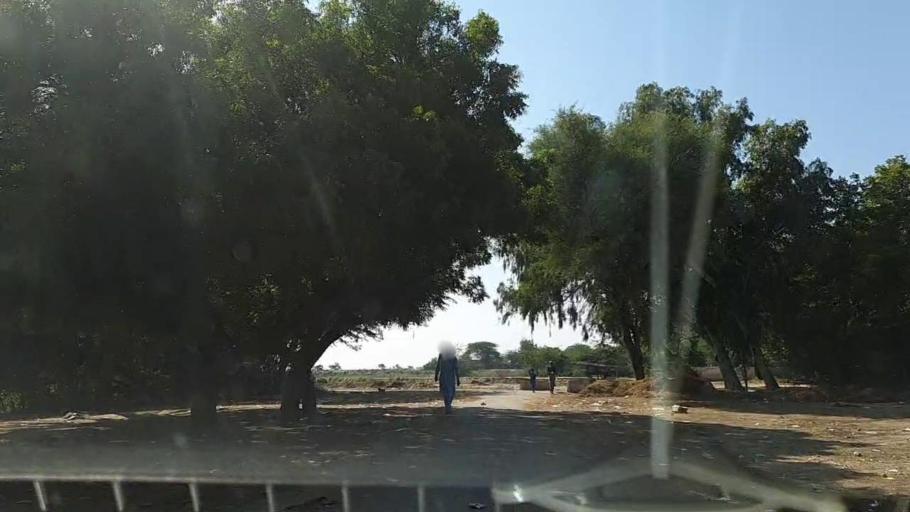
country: PK
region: Sindh
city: Chuhar Jamali
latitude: 24.5710
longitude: 68.0434
